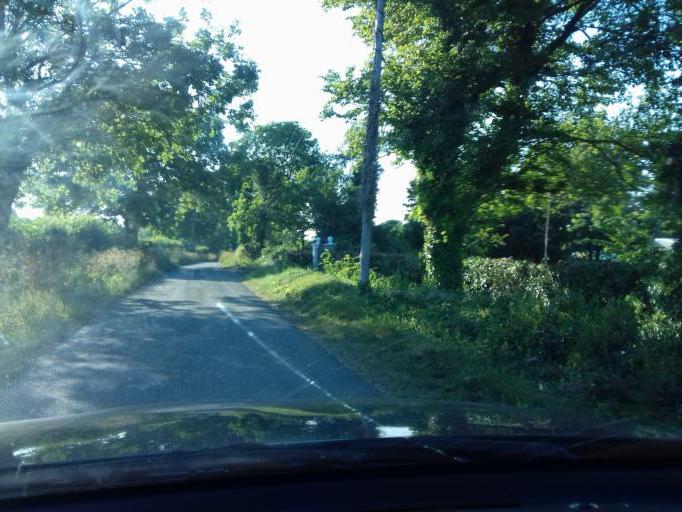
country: IE
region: Leinster
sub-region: An Mhi
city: Ashbourne
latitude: 53.4755
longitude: -6.3214
